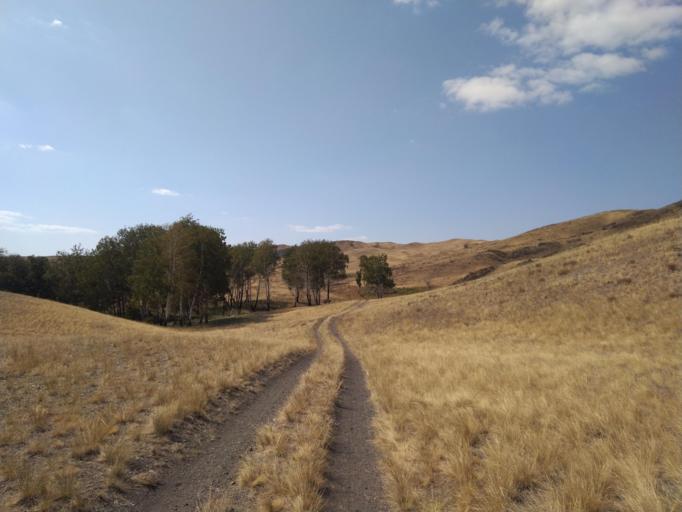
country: RU
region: Orenburg
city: Staraya Akkermanovka
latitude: 51.1938
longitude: 57.9912
